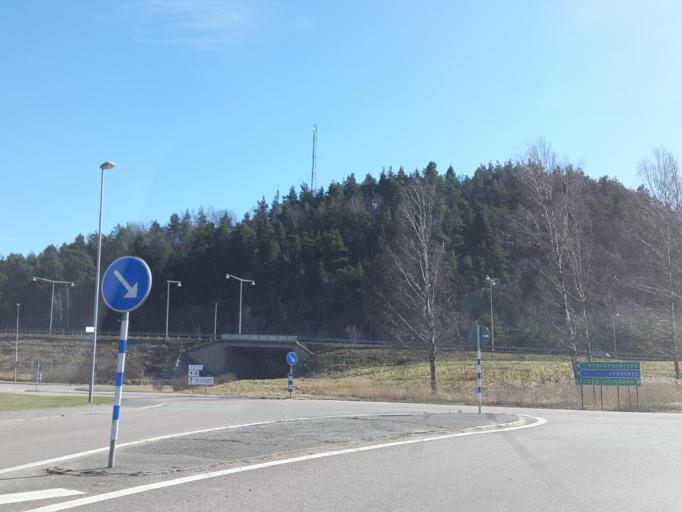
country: SE
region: Vaestra Goetaland
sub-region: Partille Kommun
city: Furulund
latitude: 57.7451
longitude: 12.1584
